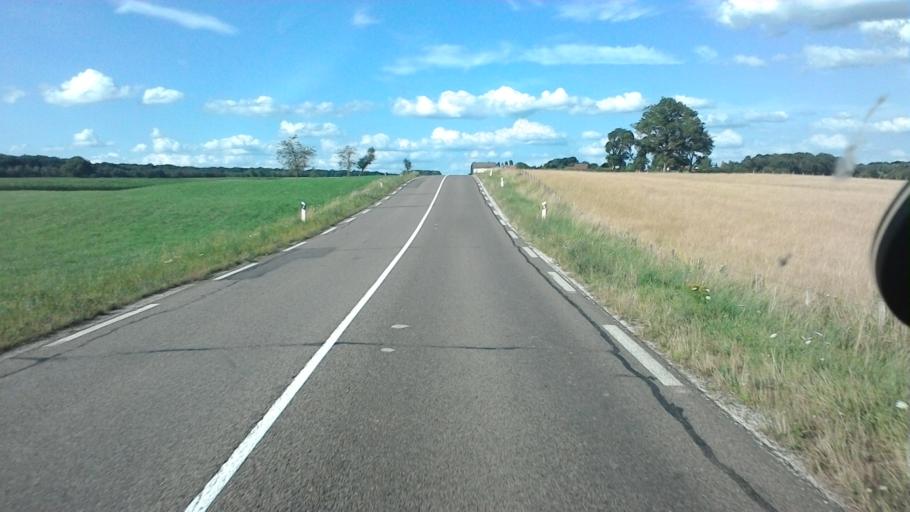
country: FR
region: Franche-Comte
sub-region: Departement de la Haute-Saone
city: Luxeuil-les-Bains
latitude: 47.7276
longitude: 6.3105
